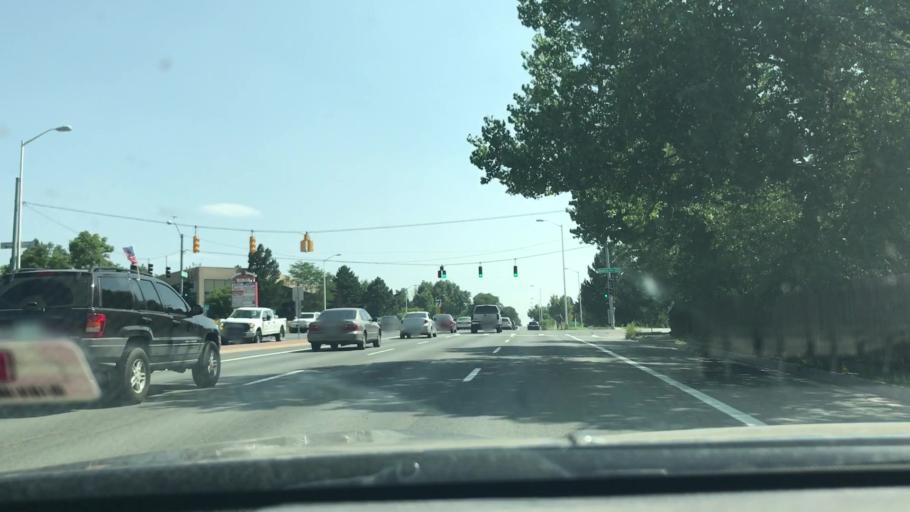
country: US
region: Colorado
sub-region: El Paso County
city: Cimarron Hills
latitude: 38.9264
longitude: -104.7754
